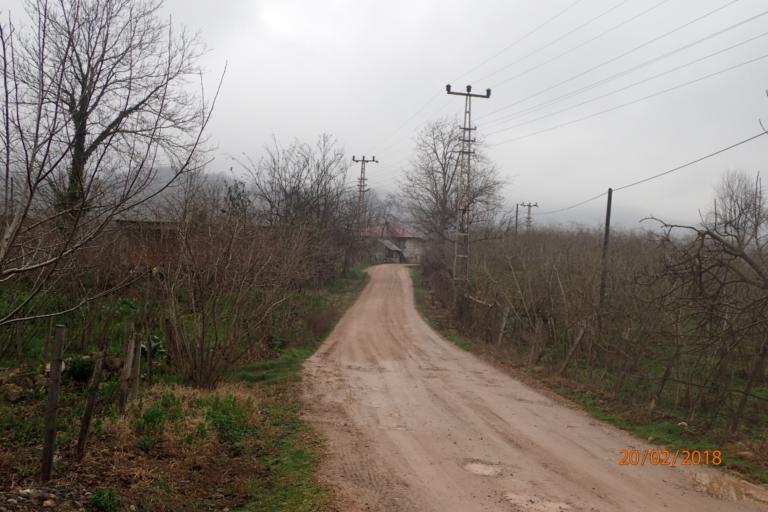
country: TR
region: Ordu
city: Camas
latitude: 40.9480
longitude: 37.5298
